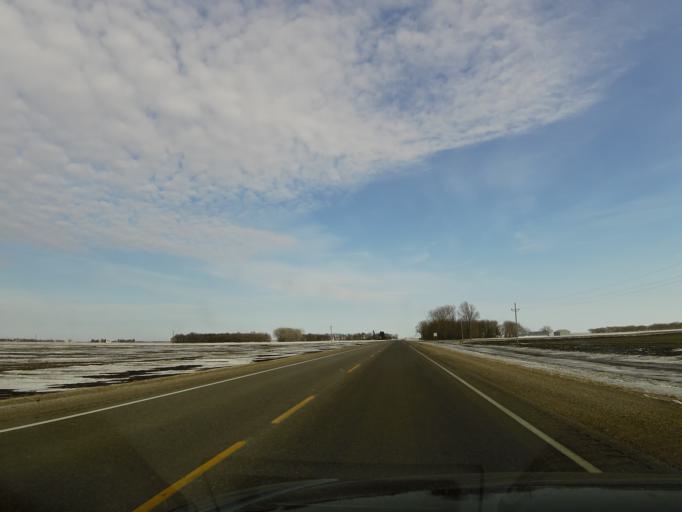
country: US
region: Minnesota
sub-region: Kittson County
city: Hallock
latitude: 48.5730
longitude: -97.1321
